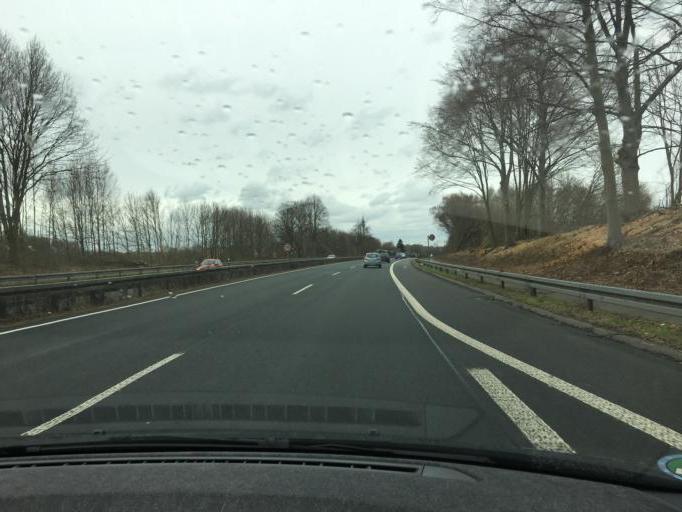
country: DE
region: North Rhine-Westphalia
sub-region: Regierungsbezirk Arnsberg
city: Dortmund
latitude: 51.4702
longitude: 7.4807
